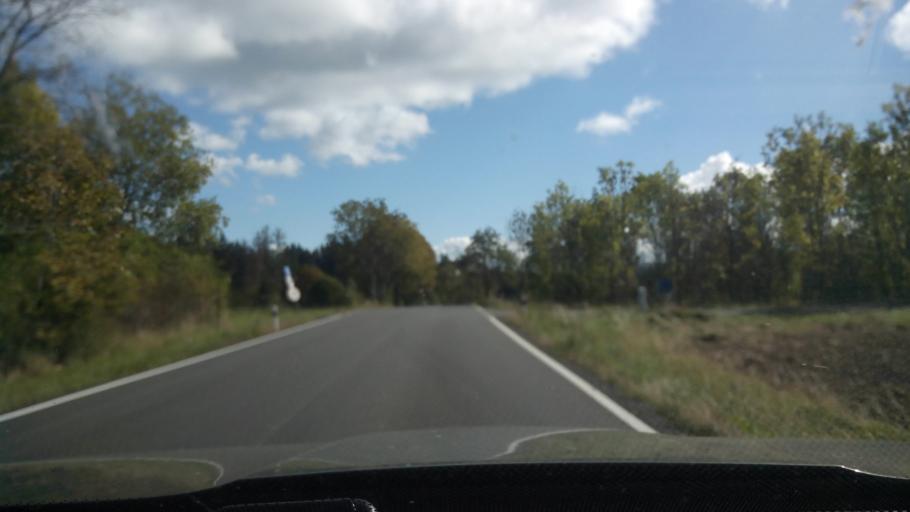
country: CZ
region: Jihocesky
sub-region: Okres Prachatice
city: Stachy
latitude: 49.1114
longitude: 13.6515
